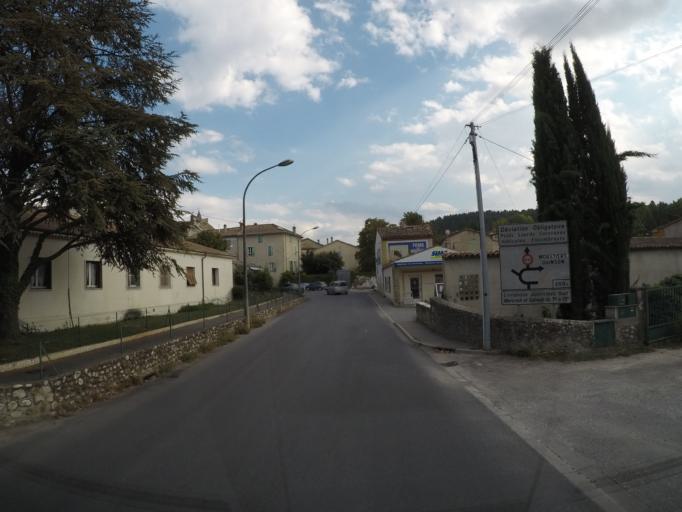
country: FR
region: Provence-Alpes-Cote d'Azur
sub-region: Departement des Alpes-de-Haute-Provence
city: Riez
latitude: 43.8188
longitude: 6.0894
